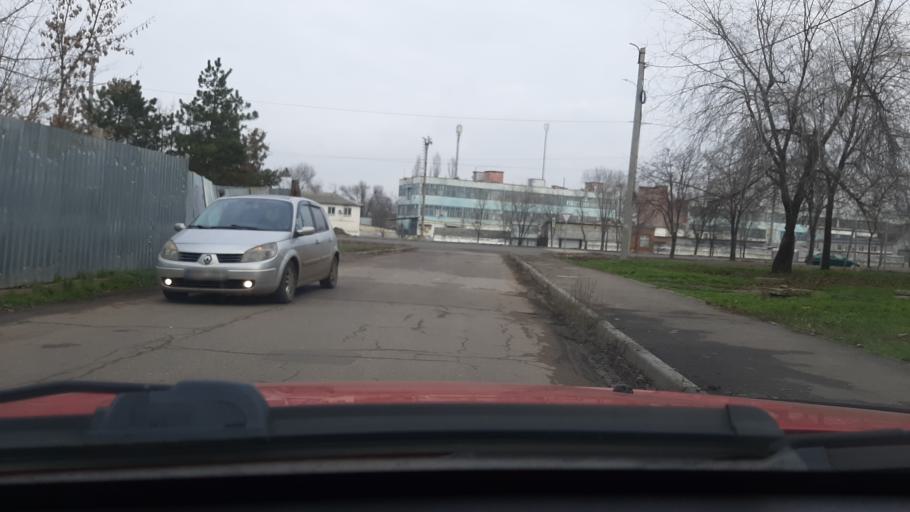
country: MD
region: Chisinau
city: Chisinau
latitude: 47.0393
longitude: 28.8367
